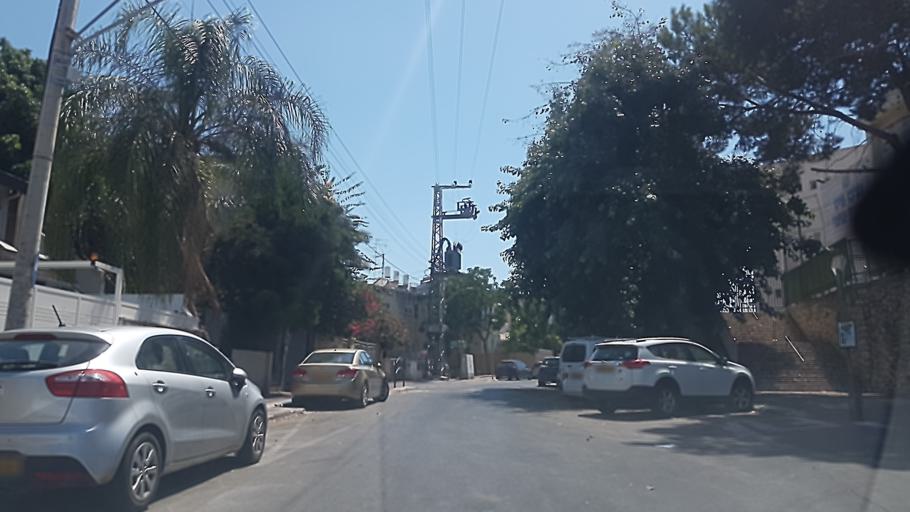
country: IL
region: Tel Aviv
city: Bene Beraq
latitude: 32.0806
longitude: 34.8246
